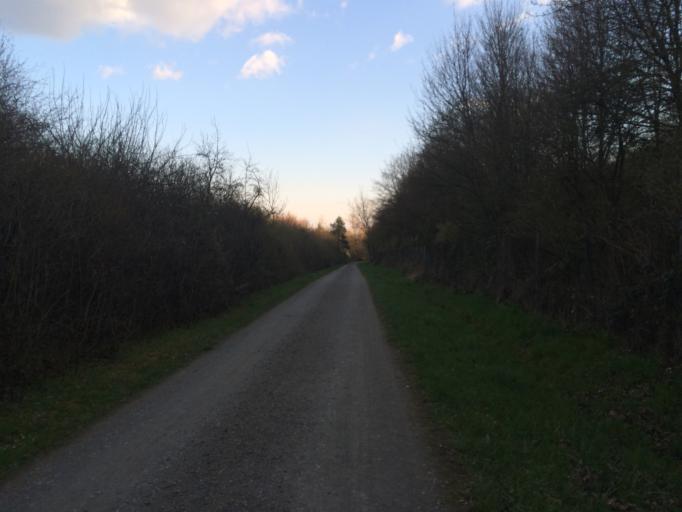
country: DE
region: Hesse
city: Morfelden-Walldorf
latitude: 49.9877
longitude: 8.5939
